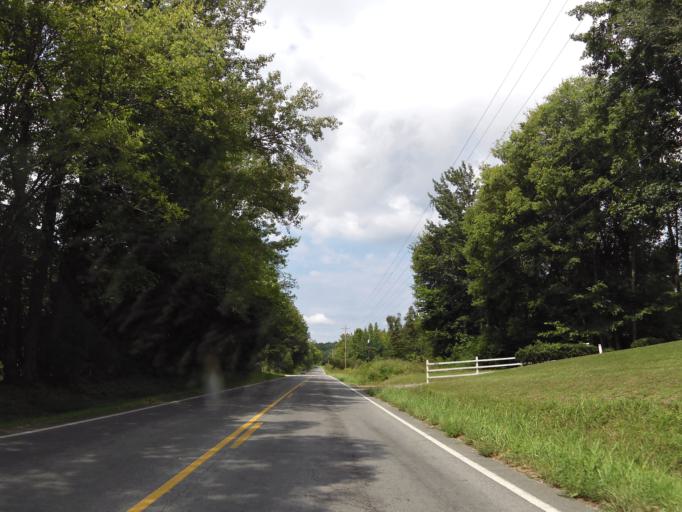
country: US
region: Tennessee
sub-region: Decatur County
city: Mount Carmel
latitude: 35.6191
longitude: -87.9747
